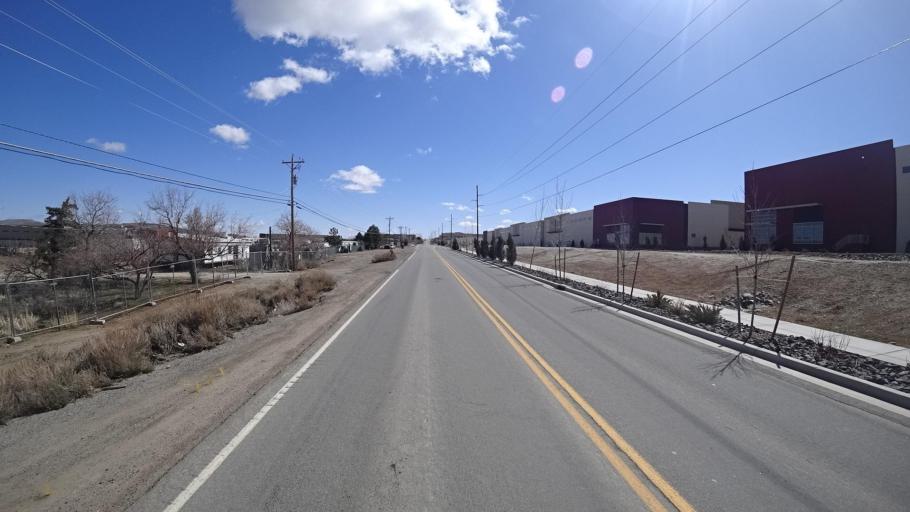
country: US
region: Nevada
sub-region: Washoe County
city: Lemmon Valley
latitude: 39.6119
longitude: -119.8729
